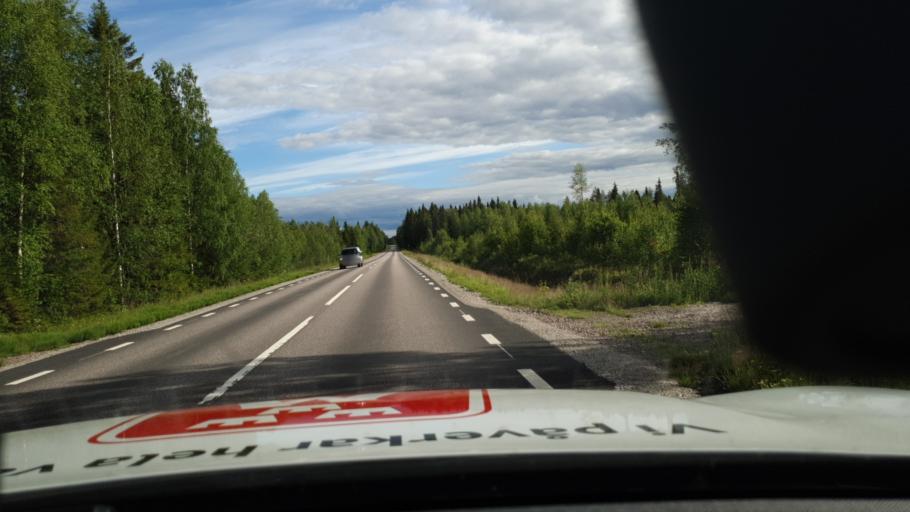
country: SE
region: Norrbotten
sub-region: Overkalix Kommun
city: OEverkalix
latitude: 66.4168
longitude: 22.8042
